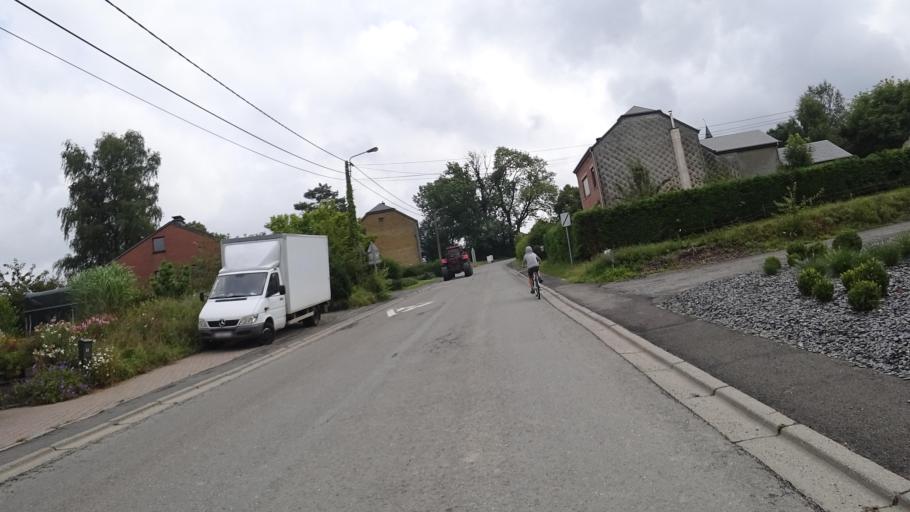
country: BE
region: Wallonia
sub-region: Province du Luxembourg
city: Chiny
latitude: 49.8182
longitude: 5.3280
